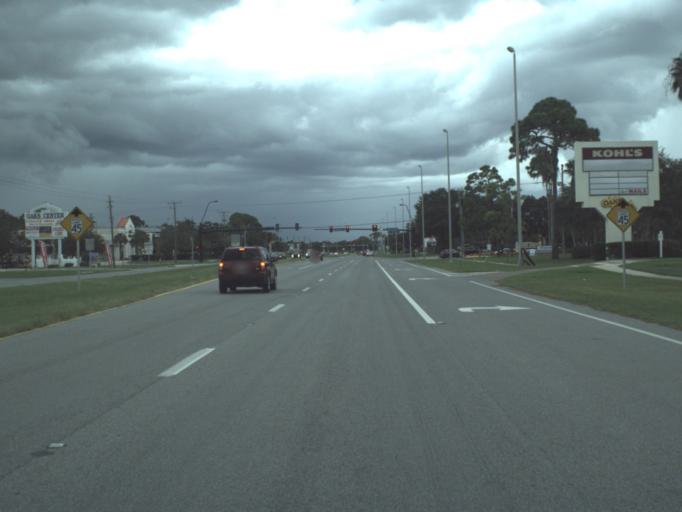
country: US
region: Florida
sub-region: Sarasota County
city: Vamo
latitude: 27.2241
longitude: -82.4924
